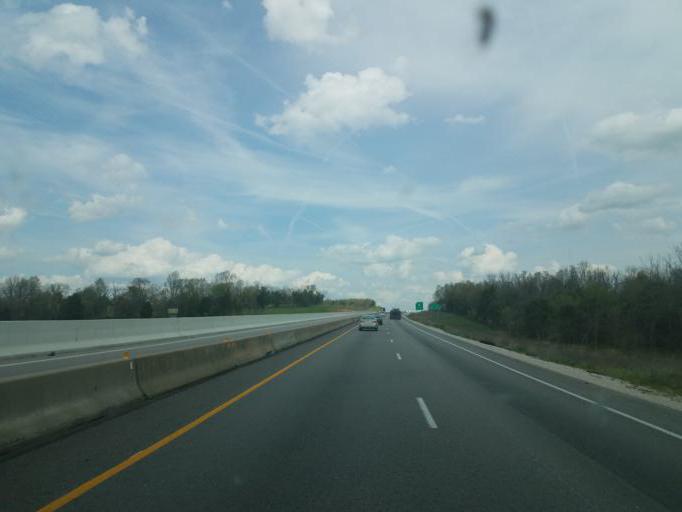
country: US
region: Kentucky
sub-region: Hart County
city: Munfordville
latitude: 37.4389
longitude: -85.8838
